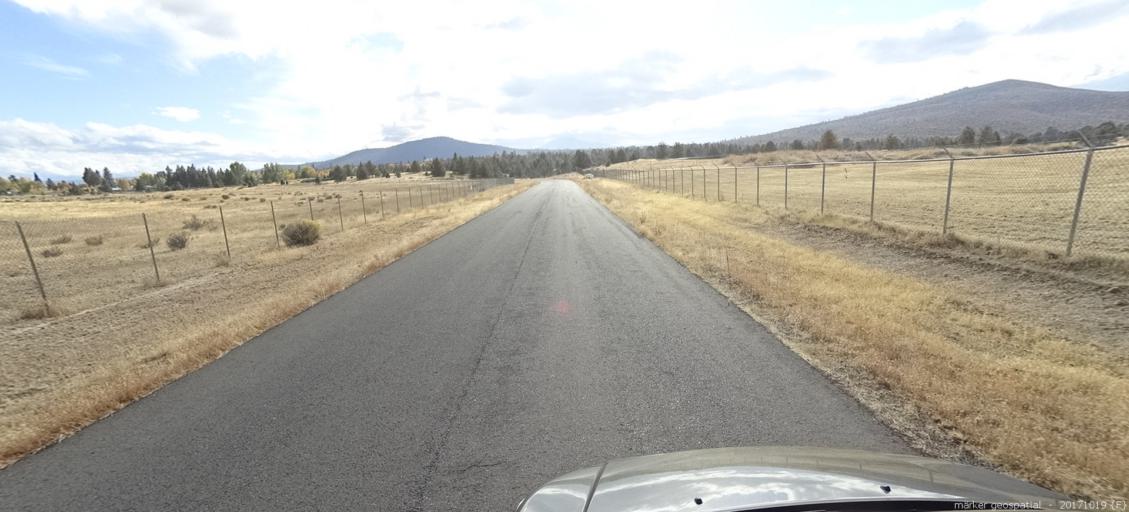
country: US
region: California
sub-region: Shasta County
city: Burney
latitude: 41.0126
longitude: -121.4409
